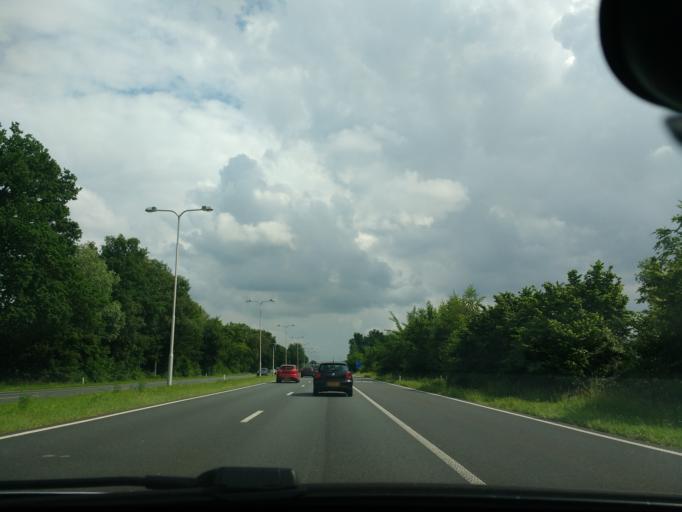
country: NL
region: Gelderland
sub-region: Gemeente Ede
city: Bennekom
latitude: 51.9981
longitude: 5.6607
